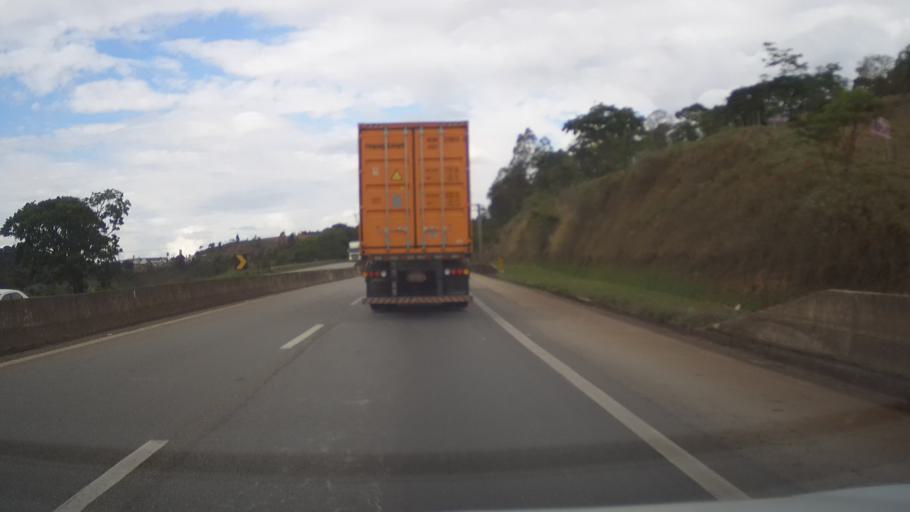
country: BR
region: Minas Gerais
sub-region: Igarape
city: Igarape
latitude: -20.2851
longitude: -44.4338
